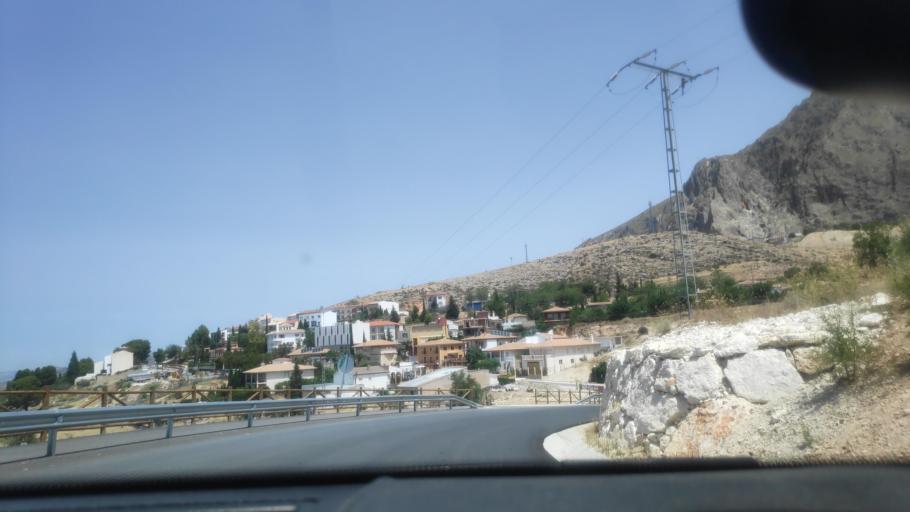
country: ES
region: Andalusia
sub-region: Provincia de Jaen
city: Jodar
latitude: 37.8144
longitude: -3.4135
